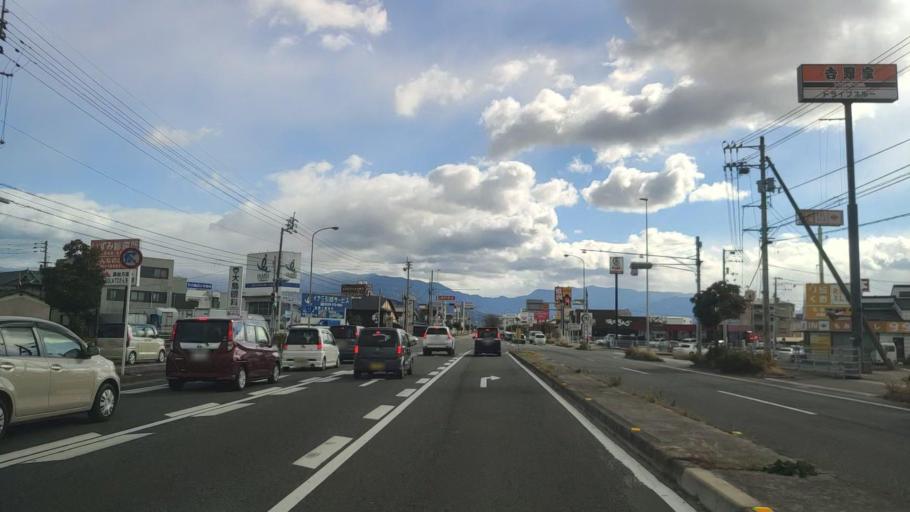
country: JP
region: Ehime
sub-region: Shikoku-chuo Shi
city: Matsuyama
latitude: 33.8150
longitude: 132.7952
